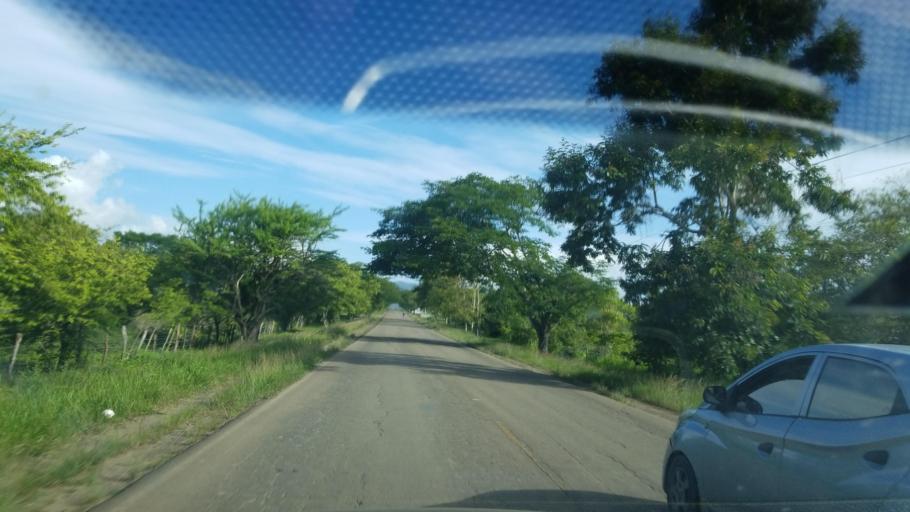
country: HN
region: El Paraiso
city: Arauli
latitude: 13.9246
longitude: -86.5579
